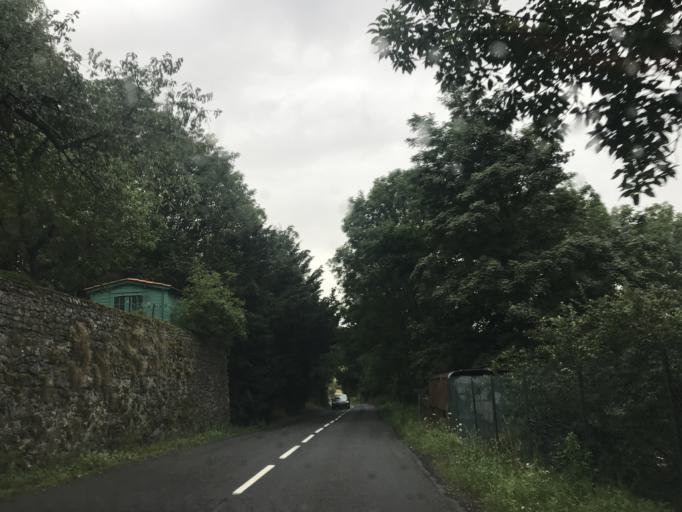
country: FR
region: Auvergne
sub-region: Departement de la Haute-Loire
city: Espaly-Saint-Marcel
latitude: 45.0599
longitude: 3.8746
